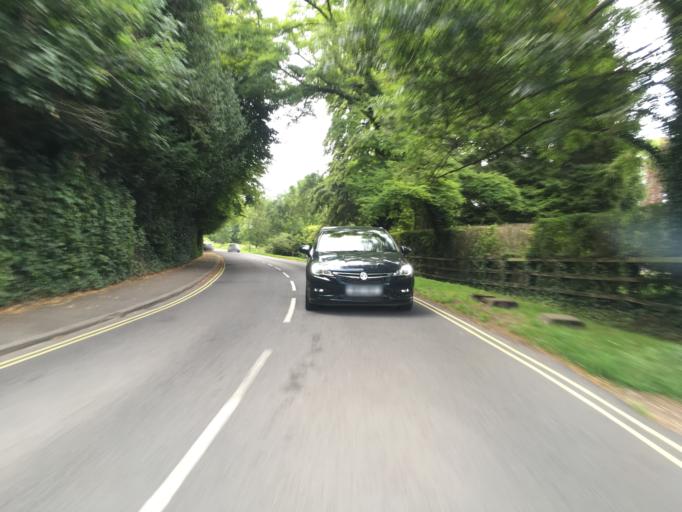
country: GB
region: England
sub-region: Hampshire
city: Compton
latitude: 51.0217
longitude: -1.3216
